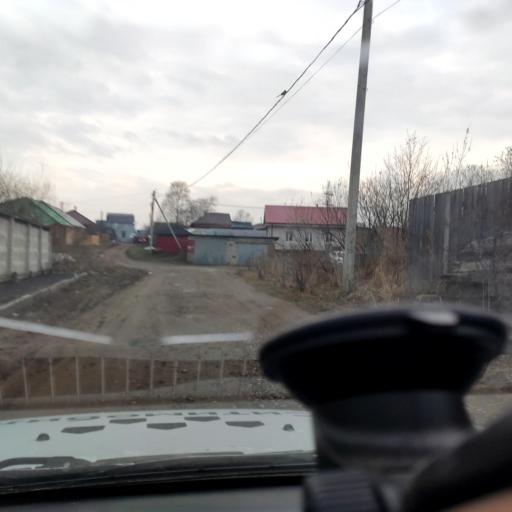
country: RU
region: Perm
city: Froly
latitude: 57.9303
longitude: 56.2350
